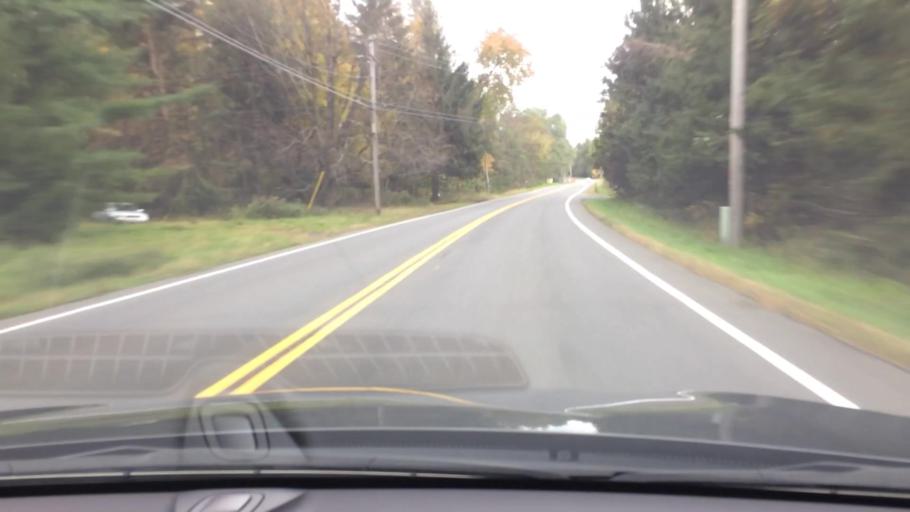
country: US
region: New York
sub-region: Columbia County
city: Lorenz Park
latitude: 42.2329
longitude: -73.7326
